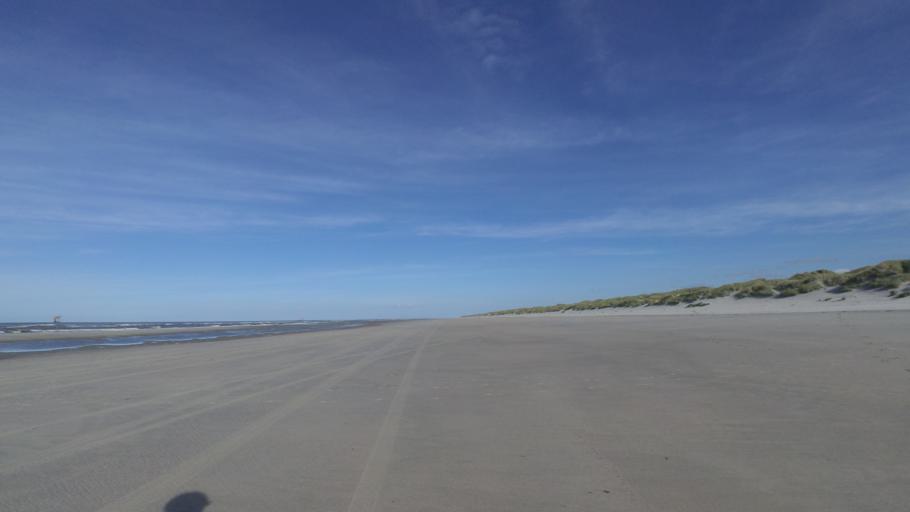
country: NL
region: Friesland
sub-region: Gemeente Ameland
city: Nes
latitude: 53.4643
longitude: 5.8392
